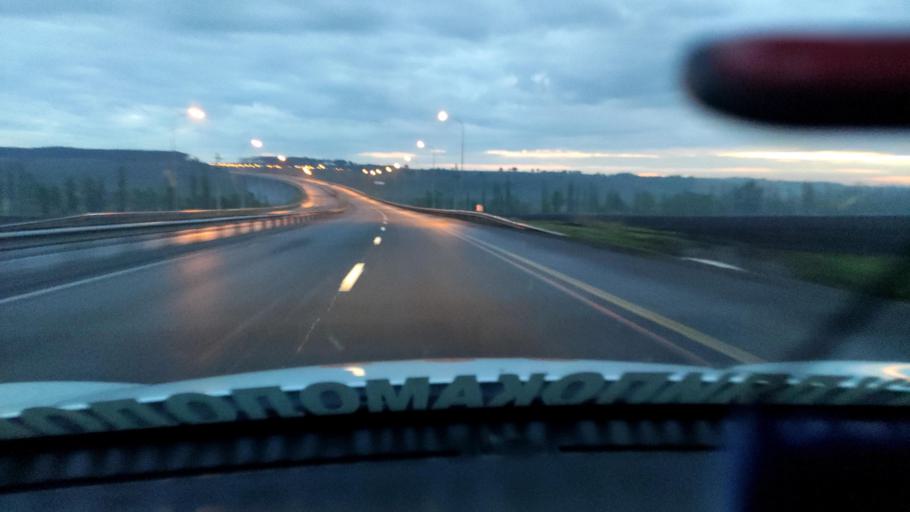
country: RU
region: Rostov
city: Tarasovskiy
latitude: 48.7239
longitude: 40.4052
